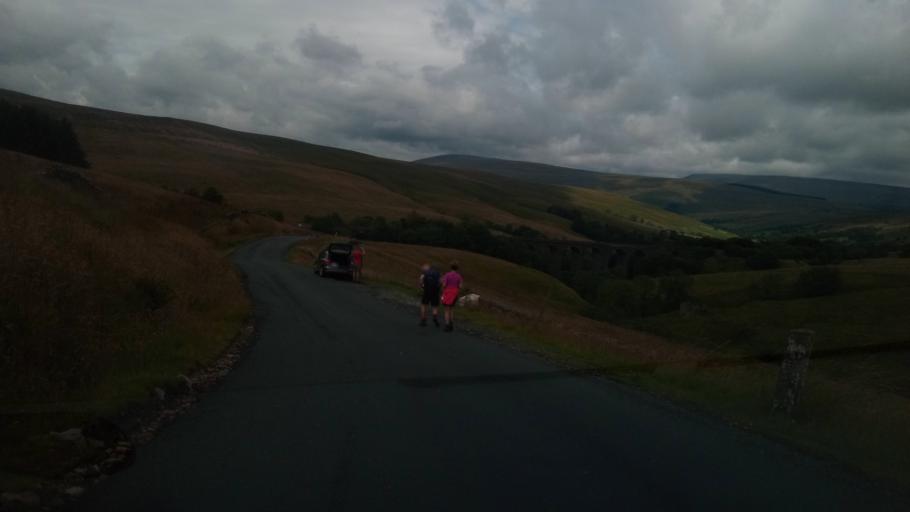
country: GB
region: England
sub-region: North Yorkshire
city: Ingleton
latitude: 54.2520
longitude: -2.3382
